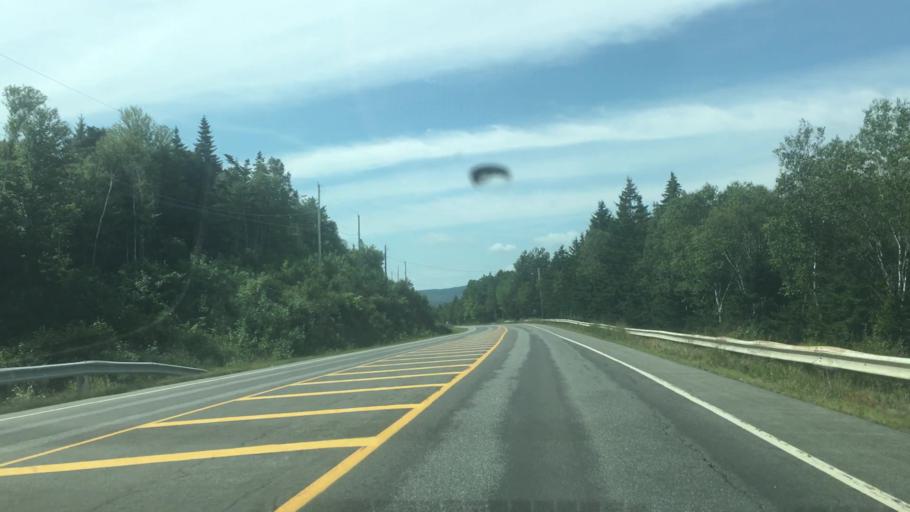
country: CA
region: Nova Scotia
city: Sydney Mines
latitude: 46.2373
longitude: -60.5663
